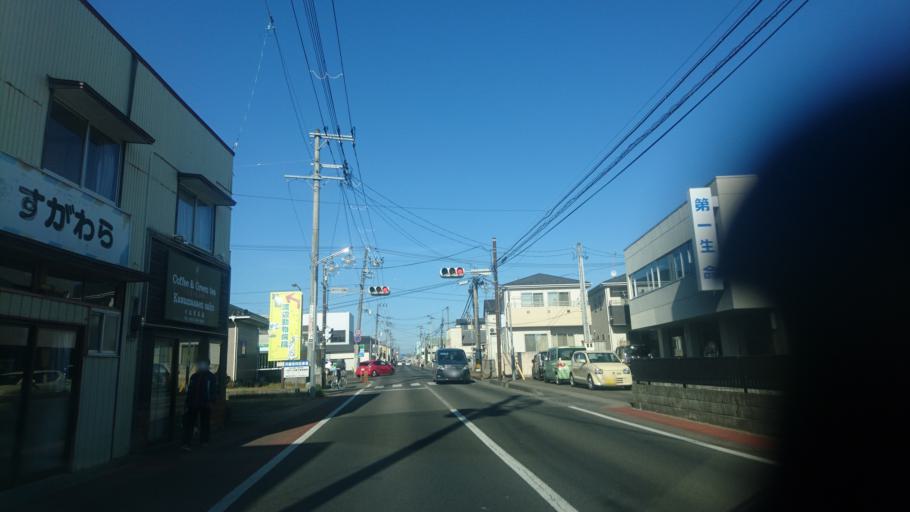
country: JP
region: Miyagi
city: Iwanuma
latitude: 38.1744
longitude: 140.8861
